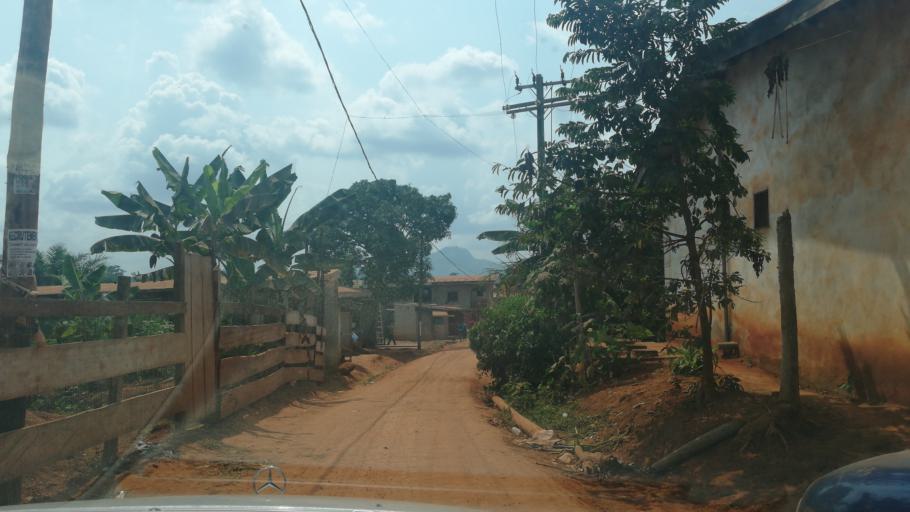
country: CM
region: Centre
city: Yaounde
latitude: 3.7843
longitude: 11.4901
